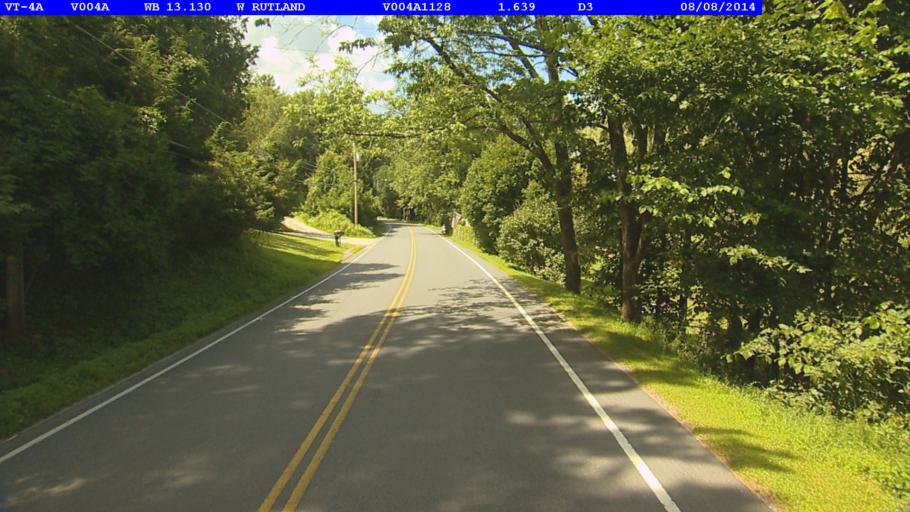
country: US
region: Vermont
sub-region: Rutland County
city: West Rutland
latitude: 43.6008
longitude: -73.0581
